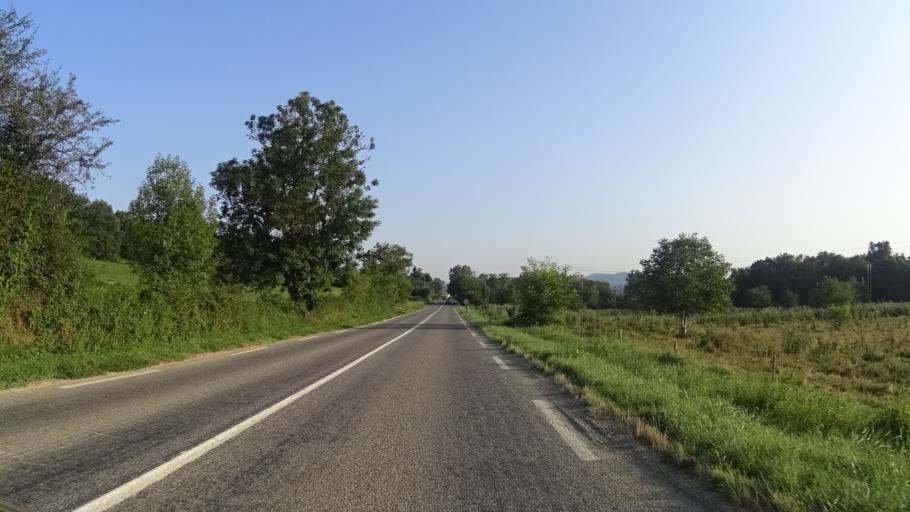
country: FR
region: Midi-Pyrenees
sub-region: Departement de l'Ariege
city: Mirepoix
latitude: 43.0748
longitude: 1.8783
